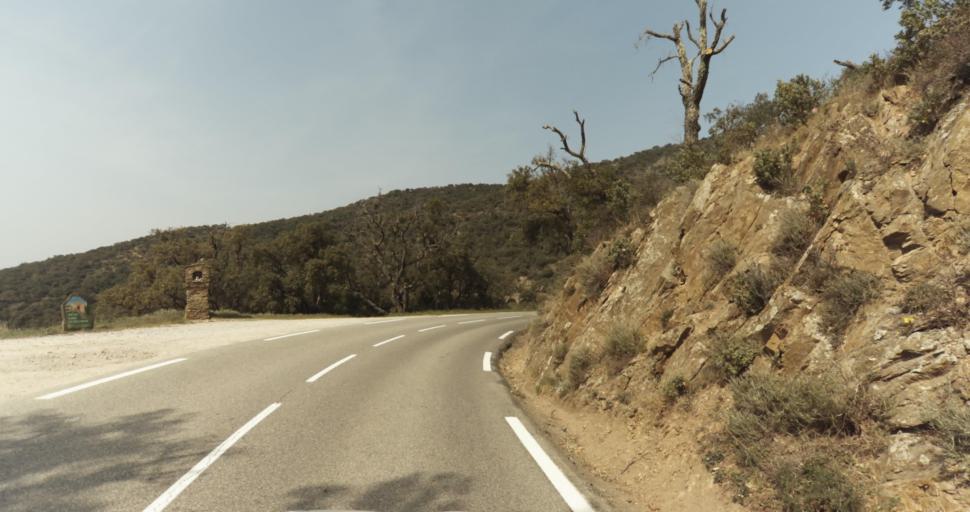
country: FR
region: Provence-Alpes-Cote d'Azur
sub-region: Departement du Var
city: Bormes-les-Mimosas
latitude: 43.1611
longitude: 6.3432
